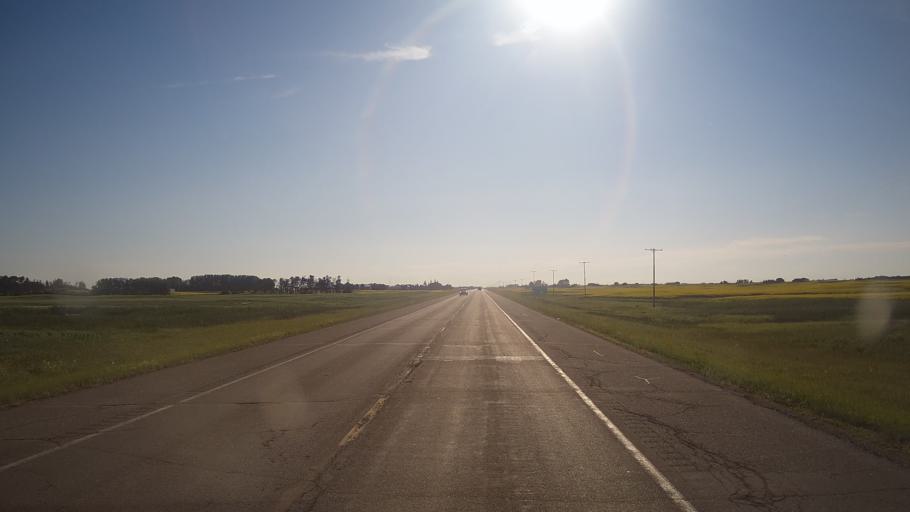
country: CA
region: Saskatchewan
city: Lanigan
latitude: 51.7944
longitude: -104.7040
